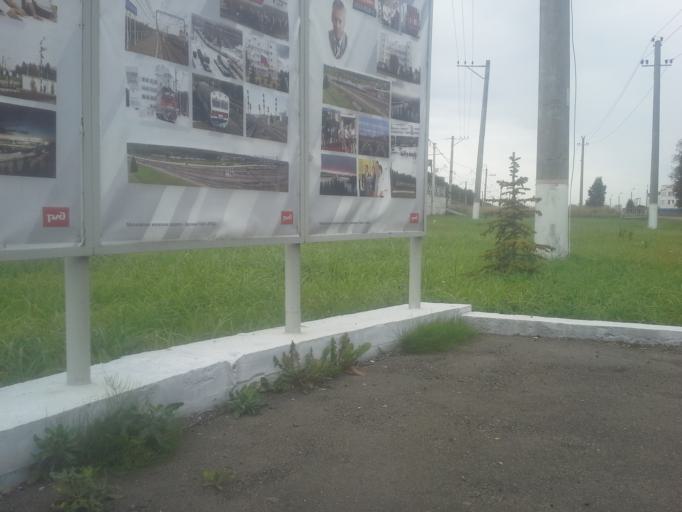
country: RU
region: Moskovskaya
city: Kievskij
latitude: 55.4052
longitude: 36.8850
